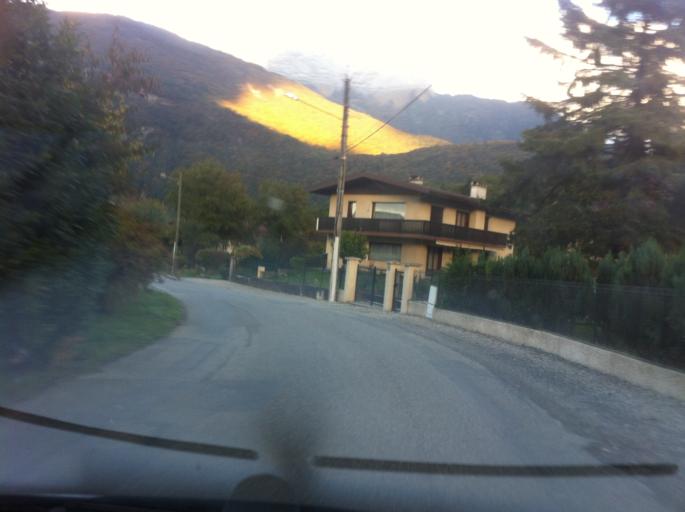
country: FR
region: Rhone-Alpes
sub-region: Departement de la Haute-Savoie
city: Doussard
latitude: 45.7751
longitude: 6.2277
